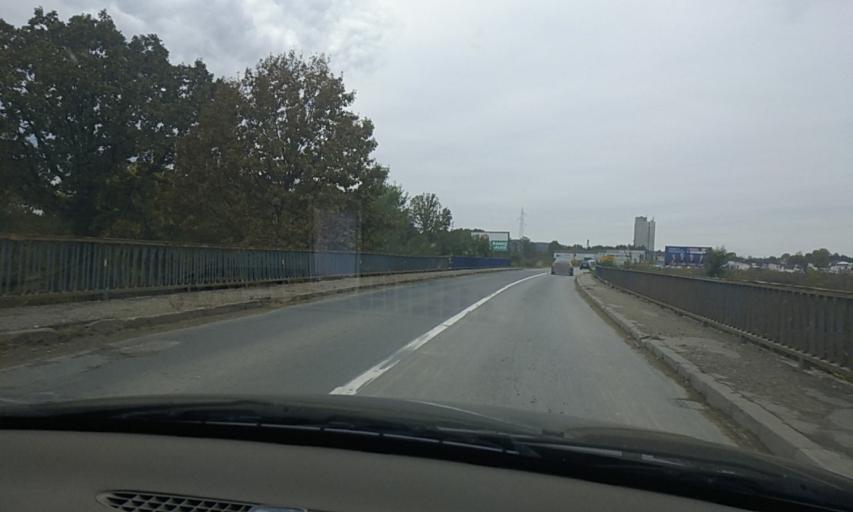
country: BA
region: Republika Srpska
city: Prnjavor
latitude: 44.8553
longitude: 17.6843
